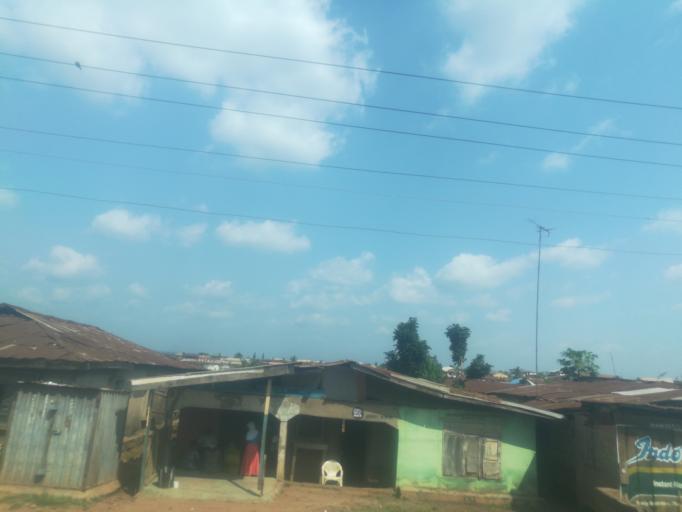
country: NG
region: Oyo
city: Moniya
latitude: 7.5259
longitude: 3.9117
